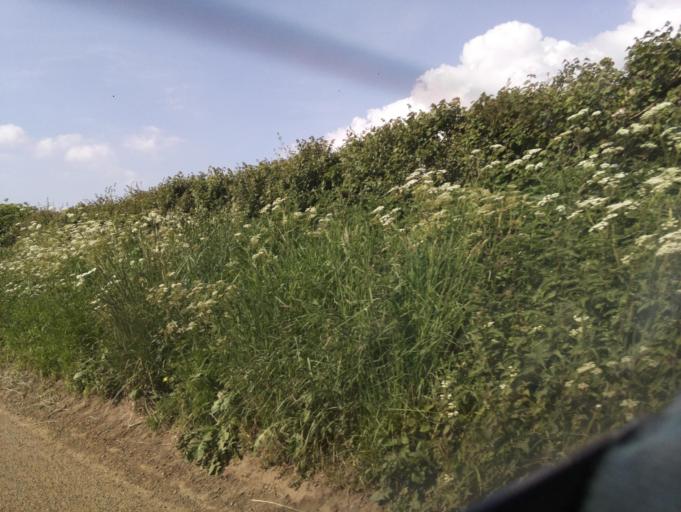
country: GB
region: England
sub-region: Wiltshire
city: Norton
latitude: 51.5475
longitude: -2.1511
